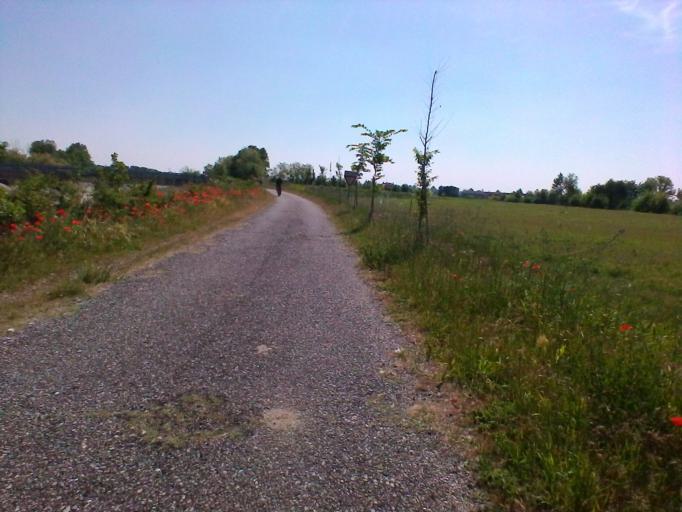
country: IT
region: Lombardy
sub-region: Provincia di Mantova
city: Soave
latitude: 45.1894
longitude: 10.7312
